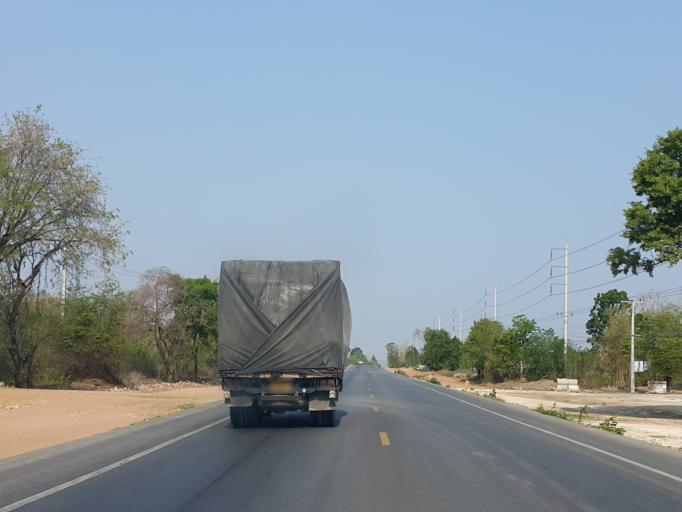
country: TH
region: Kanchanaburi
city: Sai Yok
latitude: 14.0871
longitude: 99.3488
